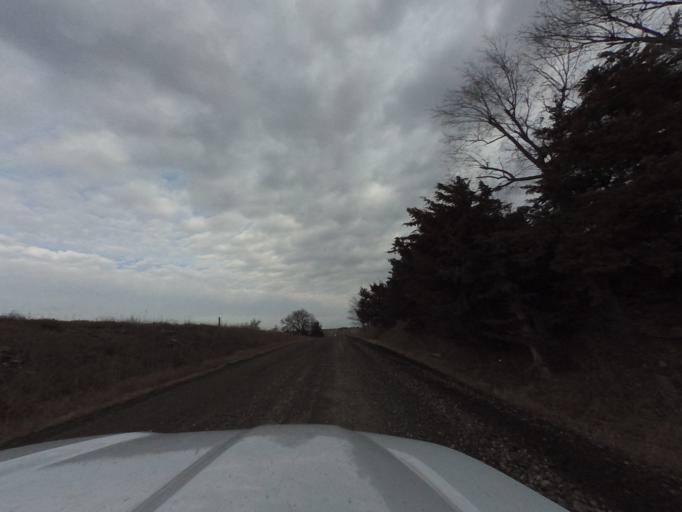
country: US
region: Kansas
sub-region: Chase County
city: Cottonwood Falls
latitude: 38.4478
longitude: -96.3731
